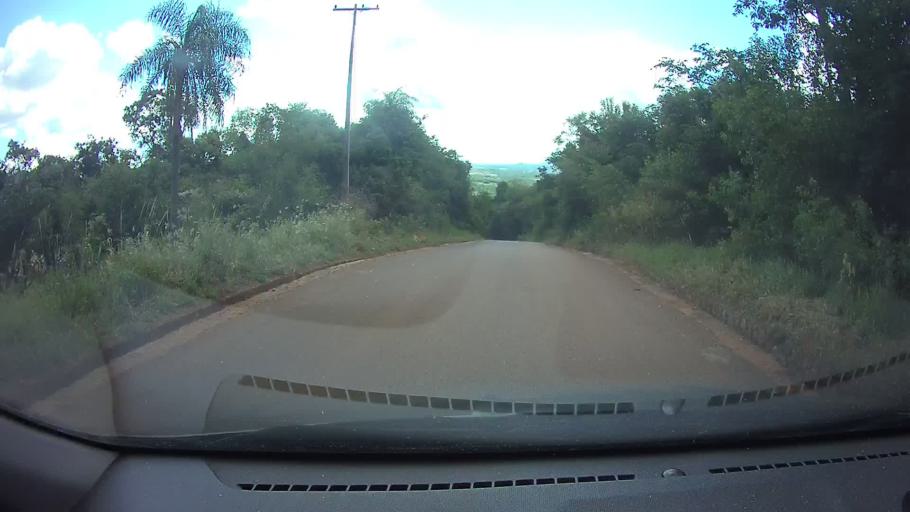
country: PY
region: Paraguari
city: La Colmena
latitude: -25.9298
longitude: -56.7848
